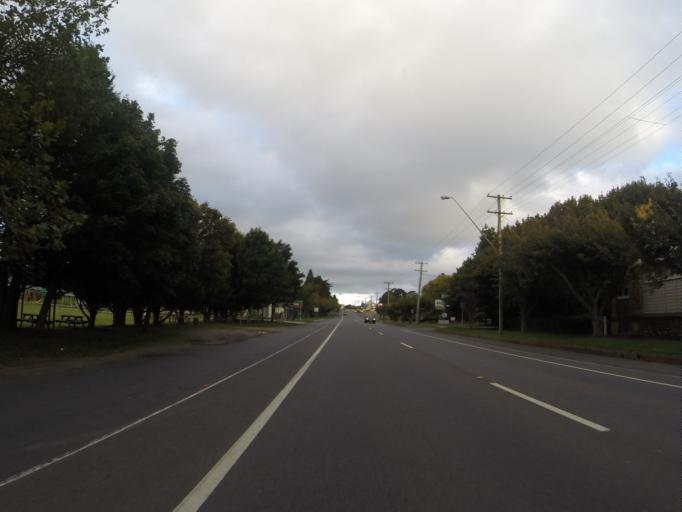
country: AU
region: New South Wales
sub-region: Shellharbour
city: Calderwood
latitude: -34.5888
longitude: 150.5935
